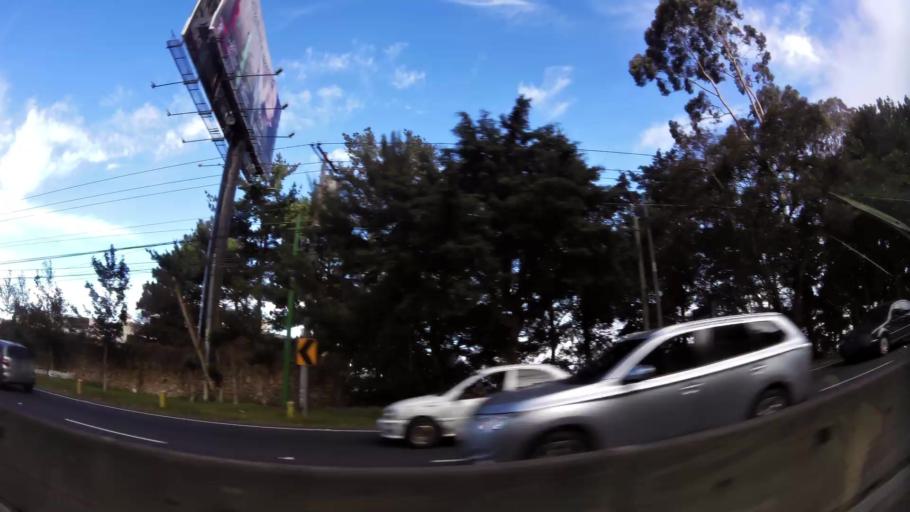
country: GT
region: Guatemala
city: Santa Catarina Pinula
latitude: 14.5764
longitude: -90.4796
